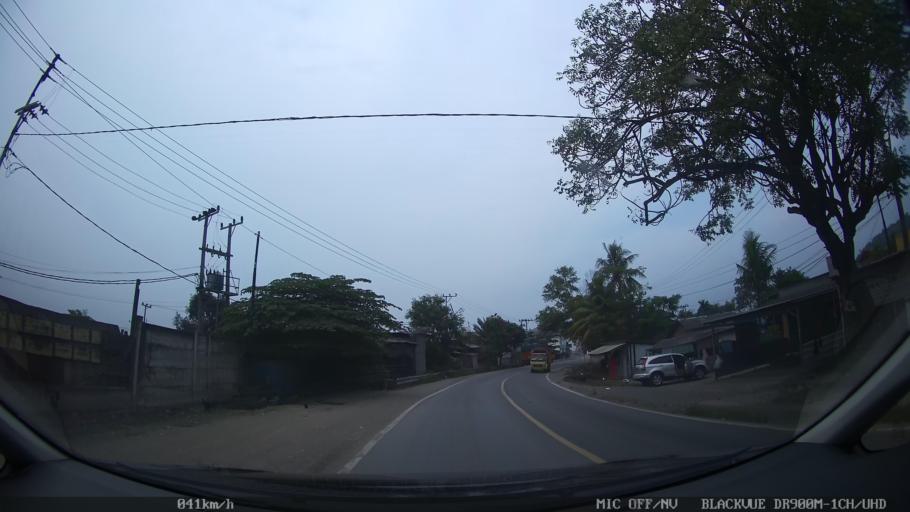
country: ID
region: Lampung
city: Panjang
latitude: -5.4362
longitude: 105.3238
